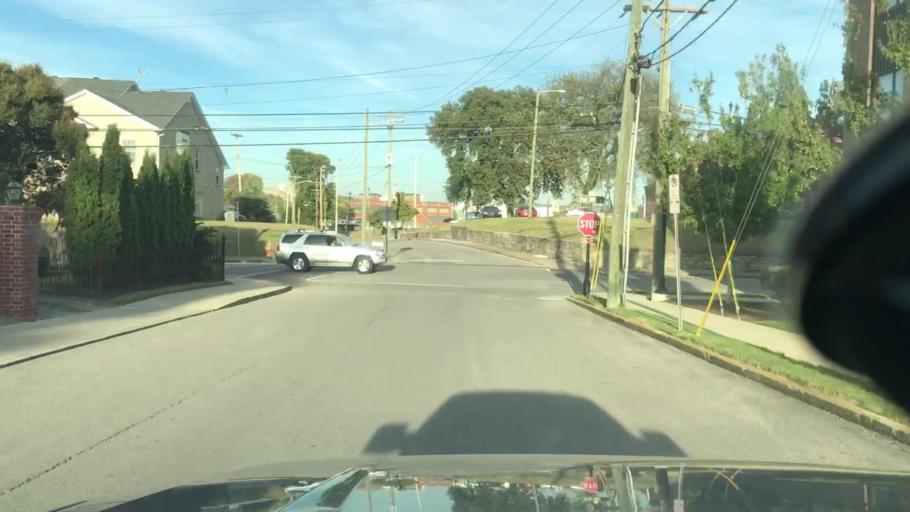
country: US
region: Tennessee
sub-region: Davidson County
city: Nashville
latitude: 36.1802
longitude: -86.7919
